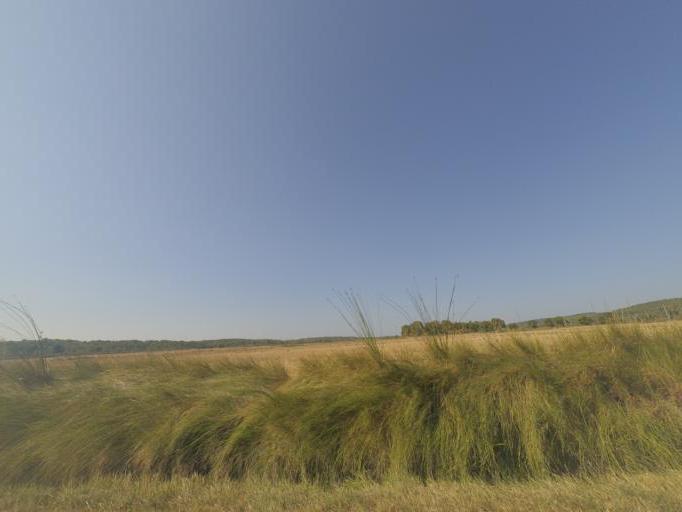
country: FR
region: Languedoc-Roussillon
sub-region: Departement du Gard
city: Calvisson
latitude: 43.7696
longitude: 4.1909
